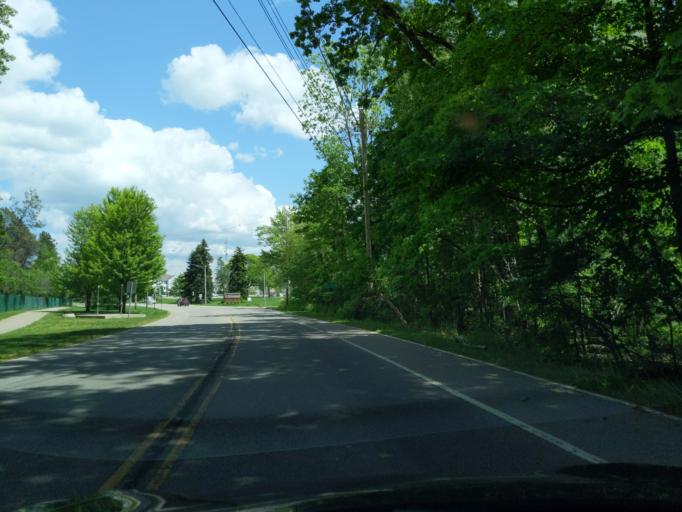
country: US
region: Michigan
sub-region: Ingham County
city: East Lansing
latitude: 42.7283
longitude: -84.5032
